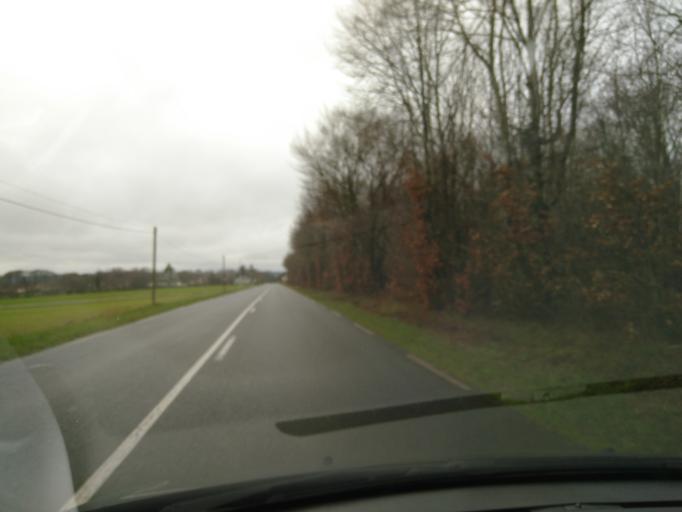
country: FR
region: Limousin
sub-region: Departement de la Haute-Vienne
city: Solignac
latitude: 45.7228
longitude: 1.2552
